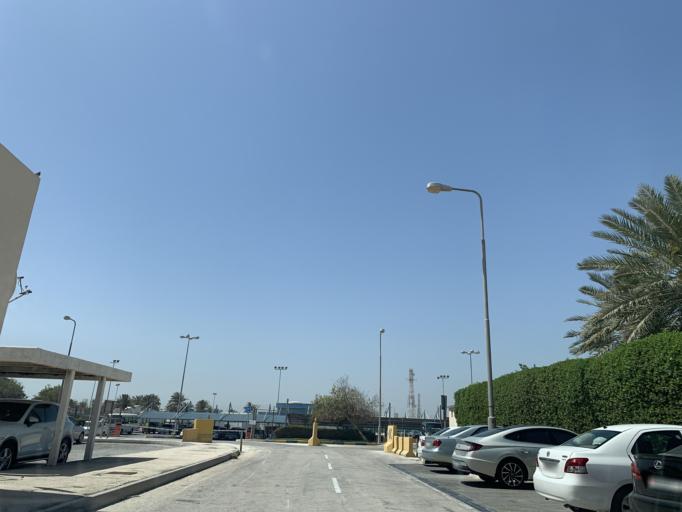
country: BH
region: Muharraq
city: Al Muharraq
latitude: 26.2732
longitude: 50.6190
